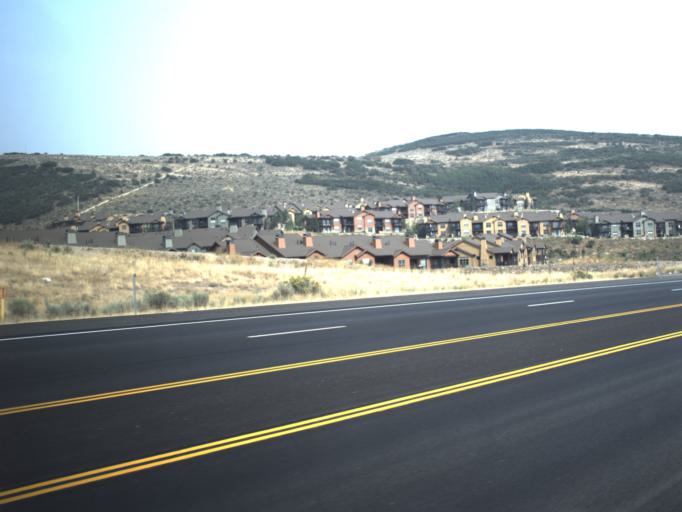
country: US
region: Utah
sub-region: Summit County
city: Park City
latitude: 40.6803
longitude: -111.4359
